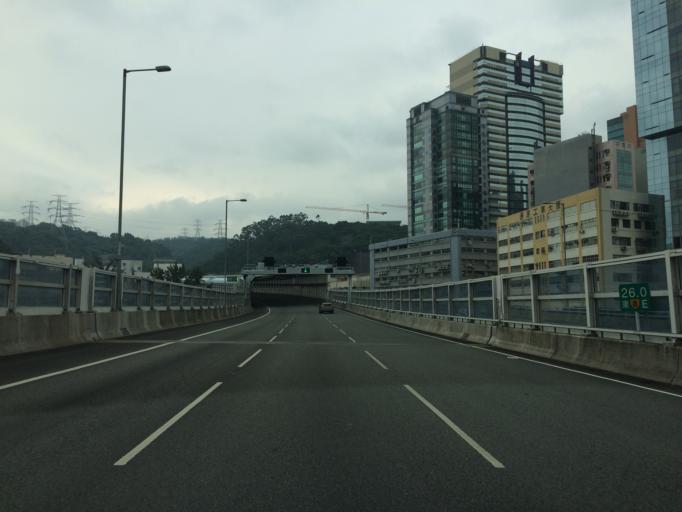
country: HK
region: Sham Shui Po
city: Sham Shui Po
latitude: 22.3359
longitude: 114.1446
